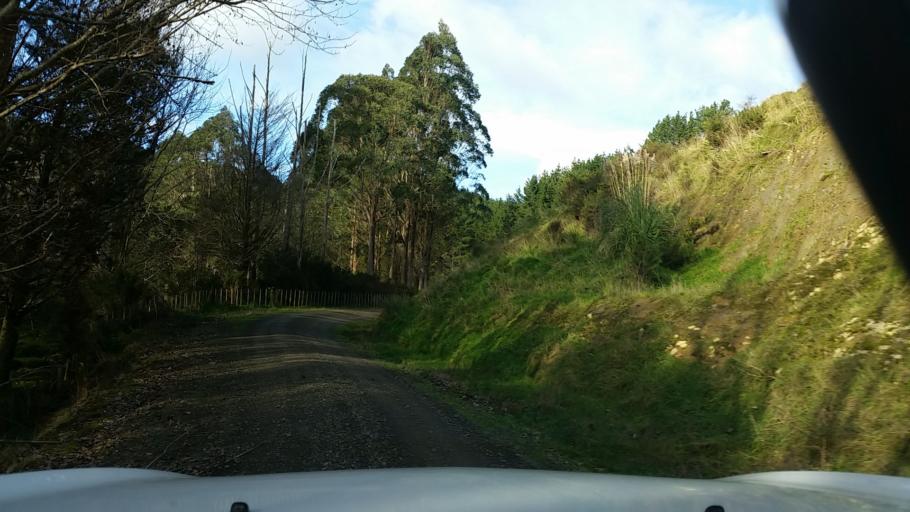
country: NZ
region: Taranaki
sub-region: New Plymouth District
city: Waitara
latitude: -38.9831
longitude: 174.4884
